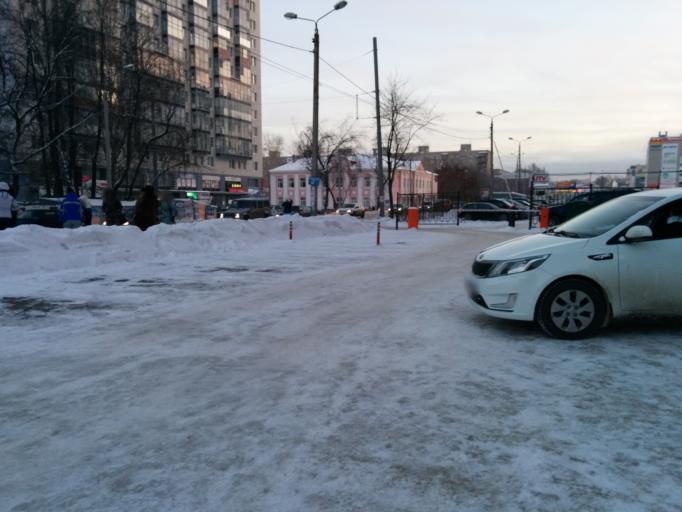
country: RU
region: Perm
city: Perm
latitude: 58.0047
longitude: 56.2665
